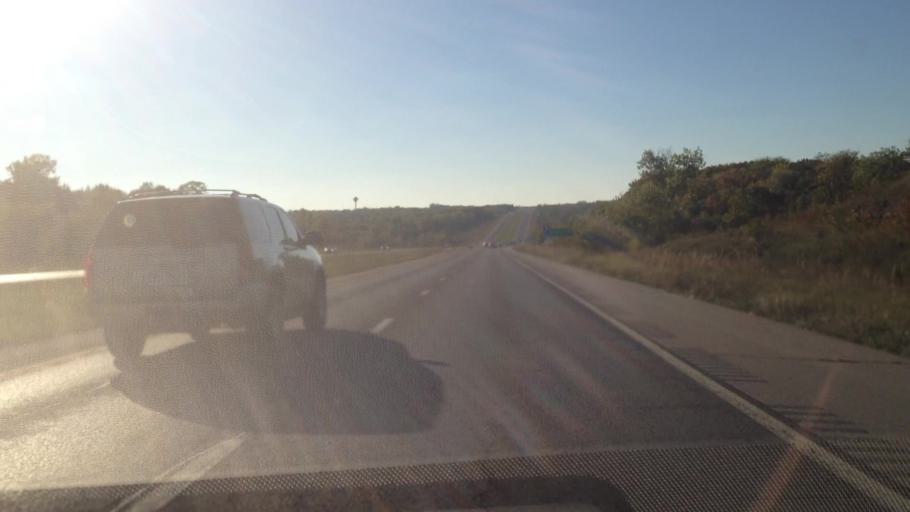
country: US
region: Kansas
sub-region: Johnson County
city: De Soto
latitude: 38.9584
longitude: -94.9643
